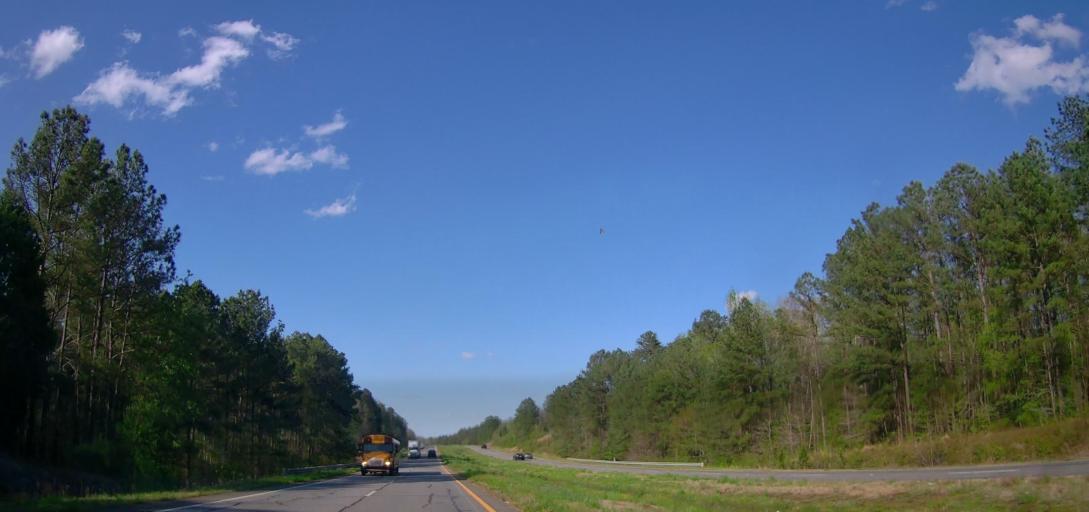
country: US
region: Georgia
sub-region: Baldwin County
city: Milledgeville
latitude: 33.0612
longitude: -83.2514
